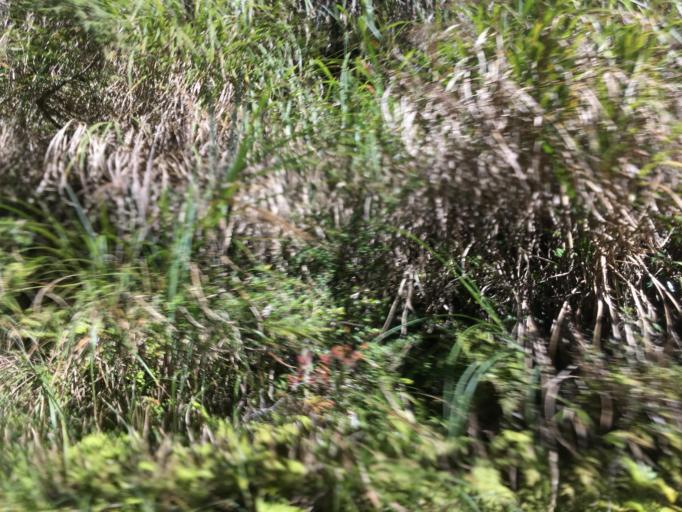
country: TW
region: Taiwan
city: Daxi
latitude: 24.5916
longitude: 121.4154
